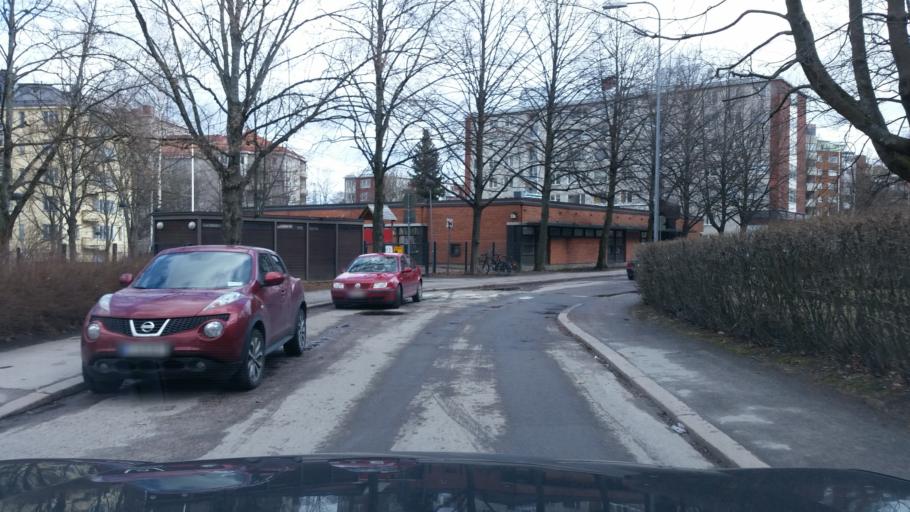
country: FI
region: Uusimaa
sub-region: Helsinki
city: Teekkarikylae
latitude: 60.1962
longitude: 24.8809
